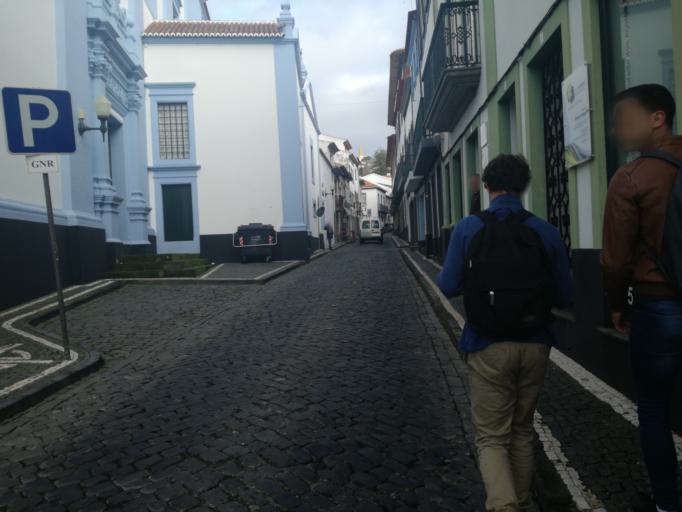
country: PT
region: Azores
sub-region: Angra do Heroismo
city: Angra do Heroismo
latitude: 38.6542
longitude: -27.2181
